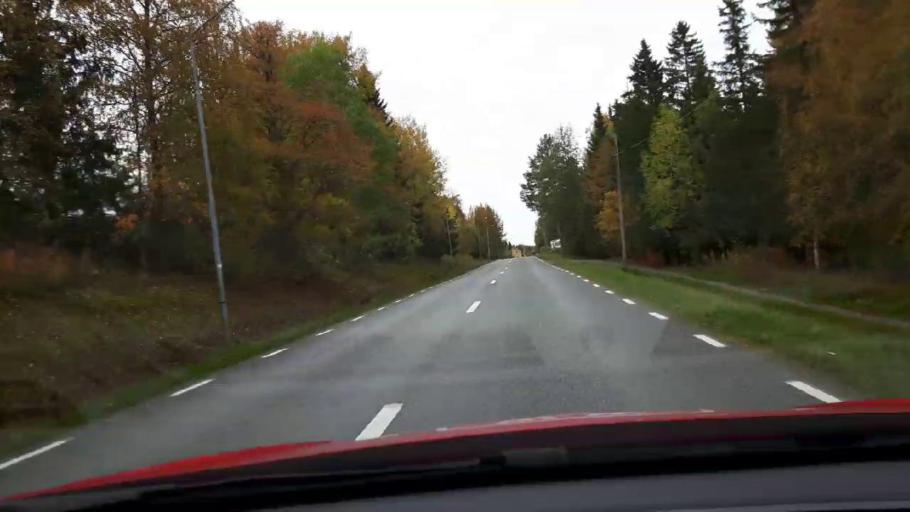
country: SE
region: Jaemtland
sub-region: Krokoms Kommun
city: Krokom
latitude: 63.1836
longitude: 14.0772
